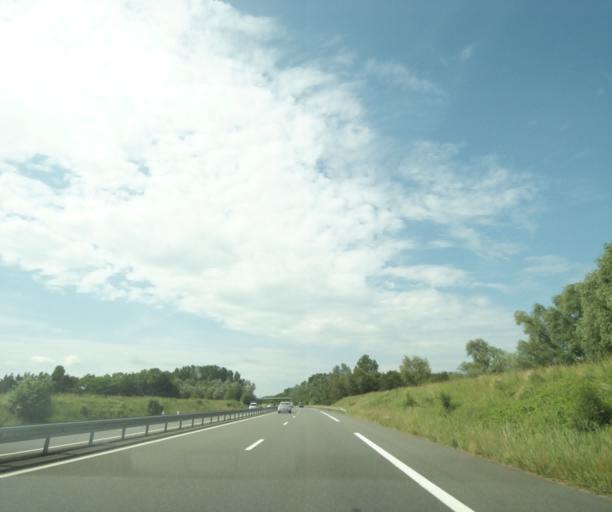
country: FR
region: Pays de la Loire
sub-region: Departement de Maine-et-Loire
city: Saint-Philbert-du-Peuple
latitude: 47.3775
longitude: -0.0853
